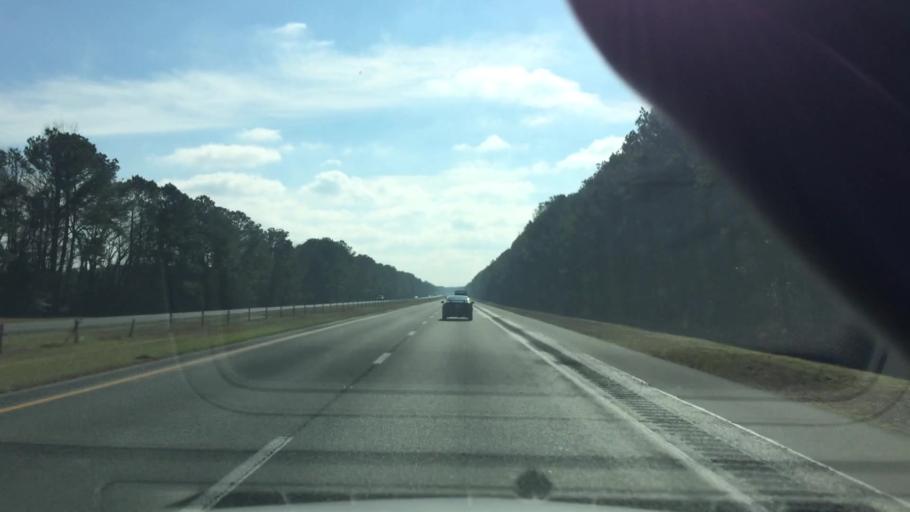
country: US
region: North Carolina
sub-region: Duplin County
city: Wallace
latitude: 34.7311
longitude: -77.9449
